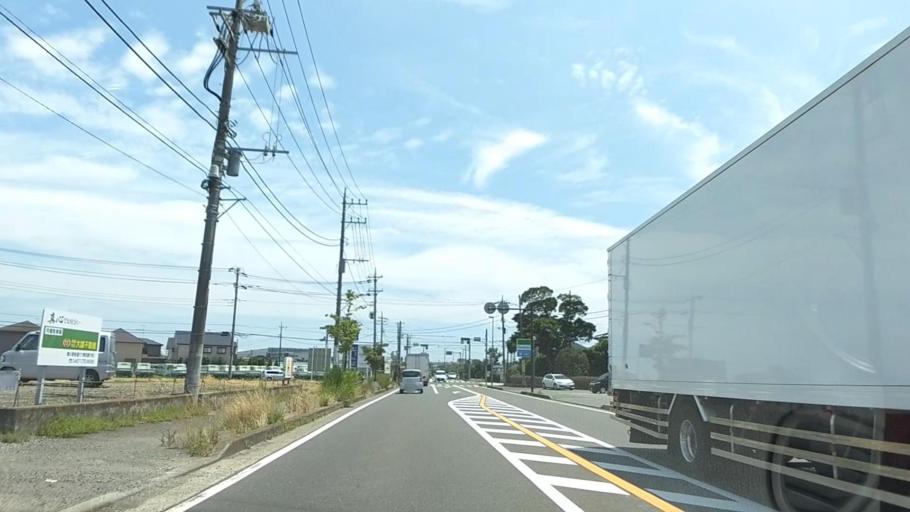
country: JP
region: Kanagawa
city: Chigasaki
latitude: 35.3825
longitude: 139.3836
